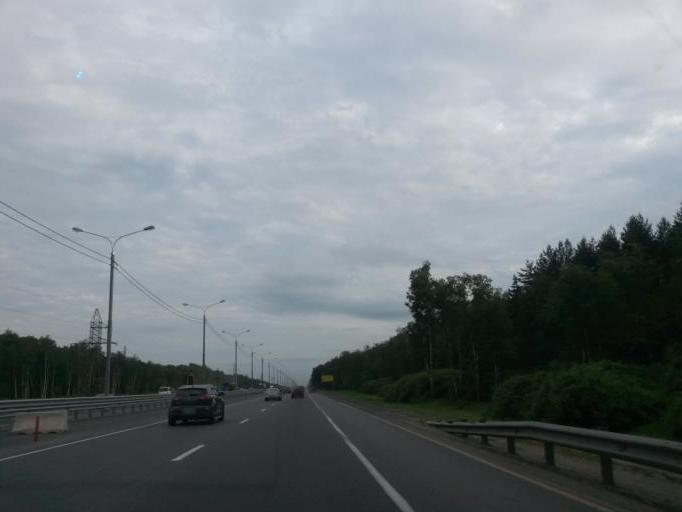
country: RU
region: Moskovskaya
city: L'vovskiy
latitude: 55.2931
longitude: 37.5443
